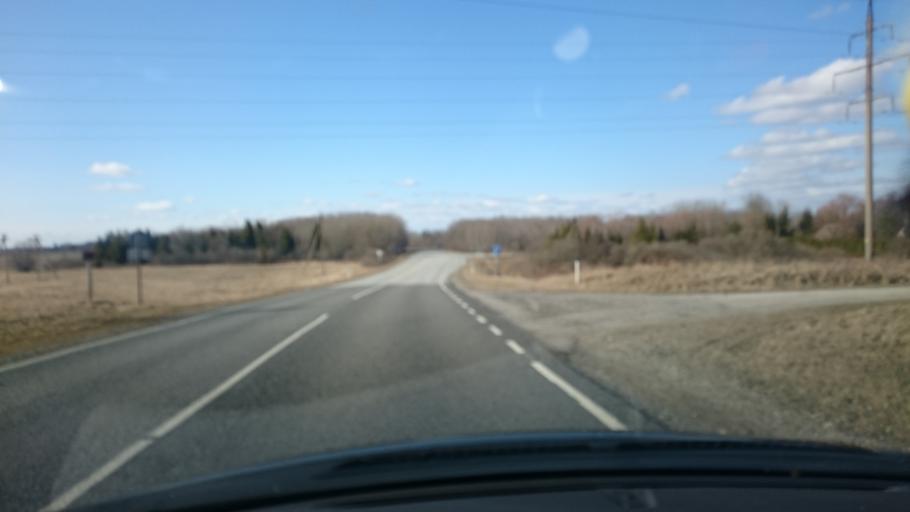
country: EE
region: Laeaene
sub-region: Lihula vald
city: Lihula
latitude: 58.6787
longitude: 23.8151
